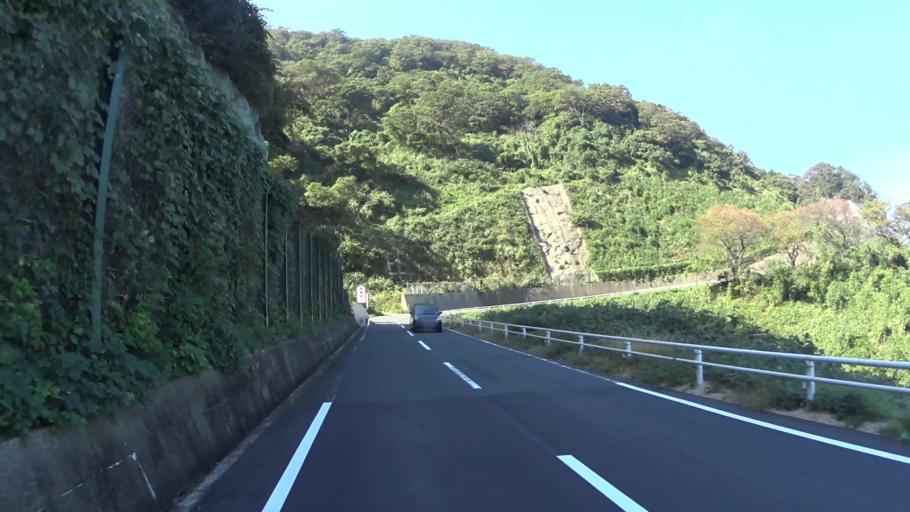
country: JP
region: Kyoto
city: Miyazu
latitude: 35.7641
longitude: 135.2351
